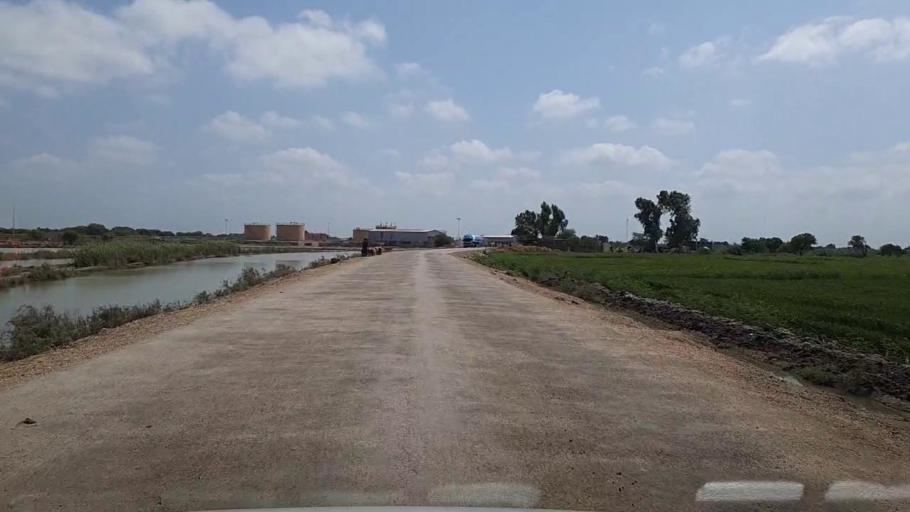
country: PK
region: Sindh
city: Talhar
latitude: 24.8800
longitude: 68.7184
